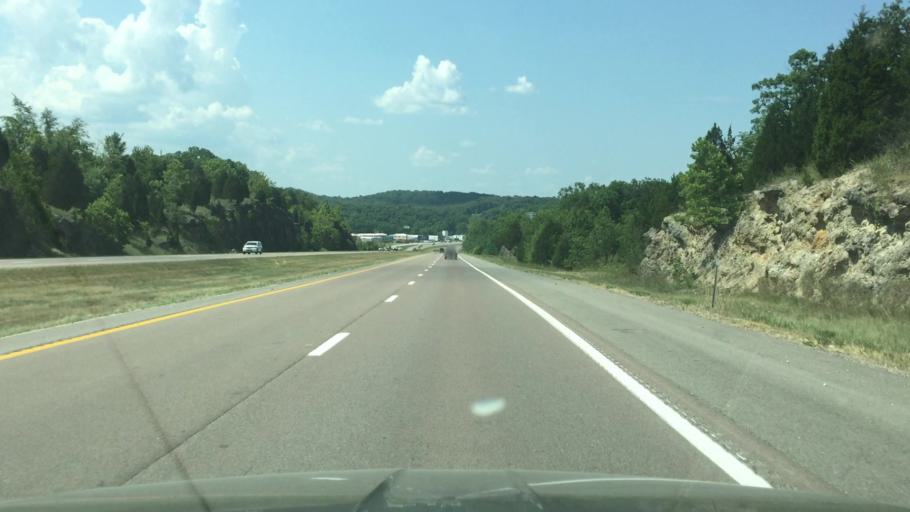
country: US
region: Missouri
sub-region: Miller County
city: Lake Ozark
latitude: 38.2536
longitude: -92.5902
